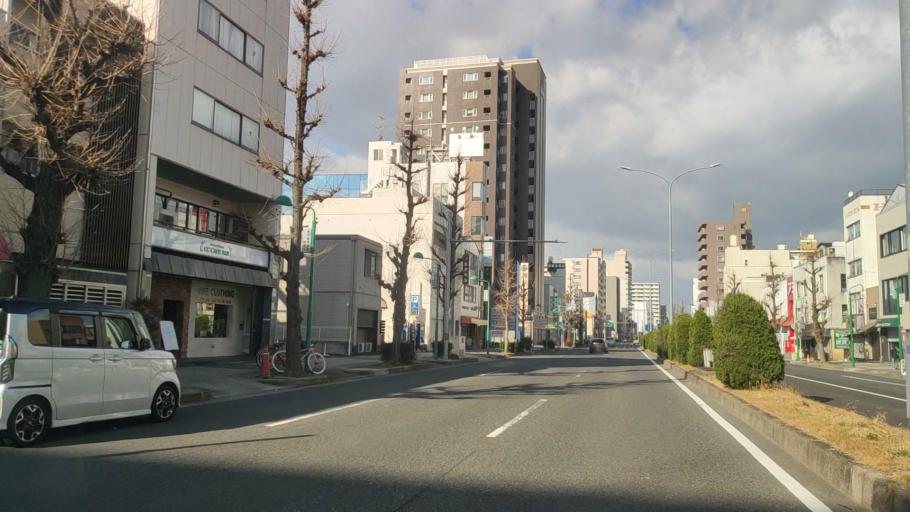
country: JP
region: Aichi
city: Nagoya-shi
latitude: 35.1575
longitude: 136.9031
